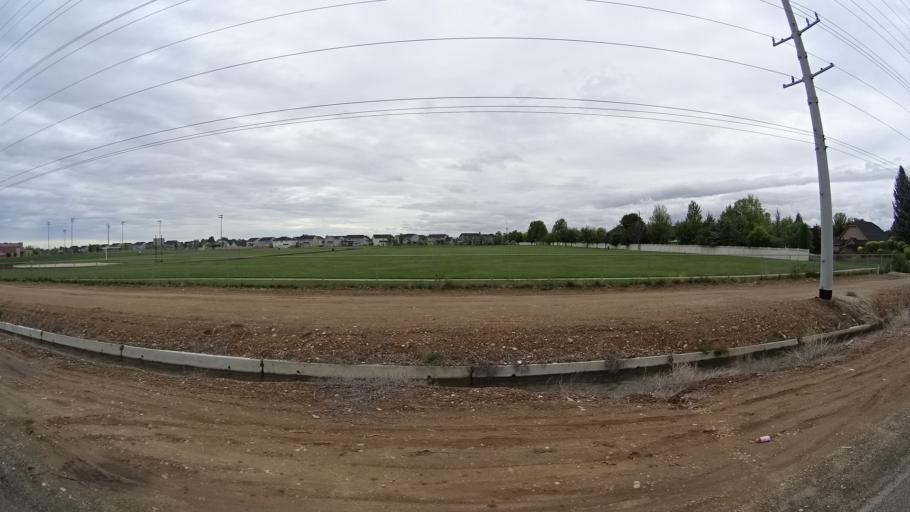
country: US
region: Idaho
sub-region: Ada County
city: Meridian
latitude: 43.6483
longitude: -116.3874
